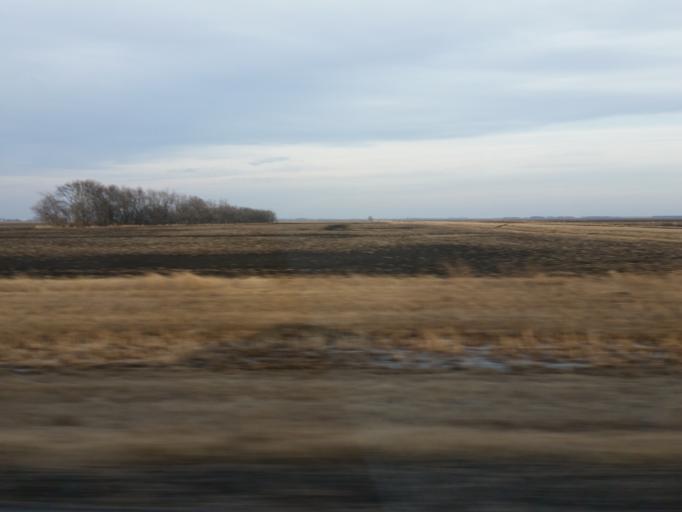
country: US
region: North Dakota
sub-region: Traill County
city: Hillsboro
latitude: 47.2826
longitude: -97.2179
